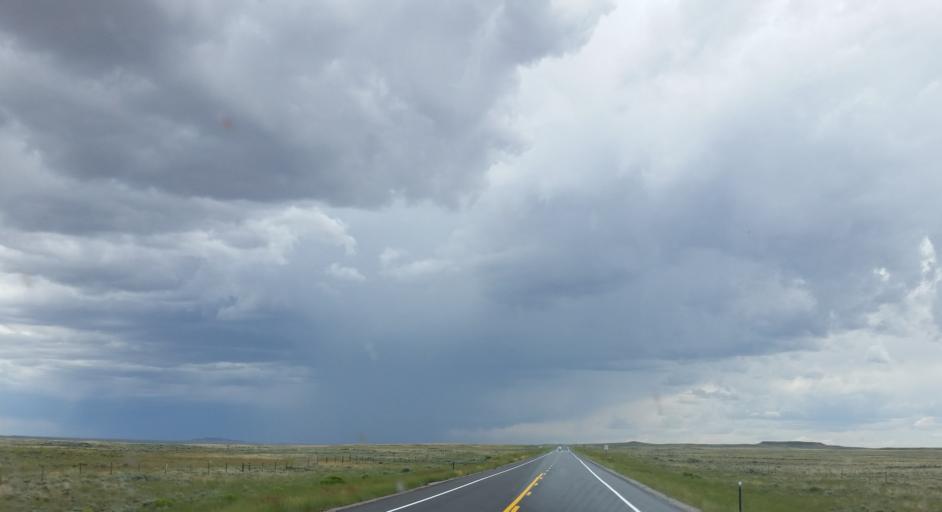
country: US
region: Wyoming
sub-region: Fremont County
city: Lander
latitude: 42.2917
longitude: -109.0442
